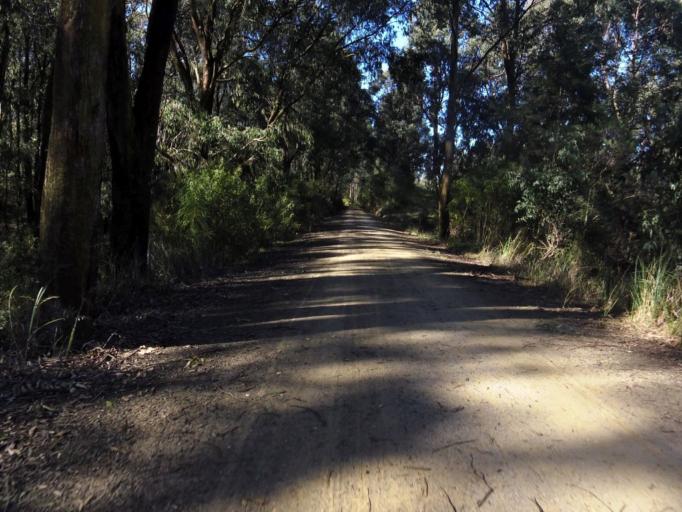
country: AU
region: Victoria
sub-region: Latrobe
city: Moe
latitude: -38.3719
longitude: 146.2027
